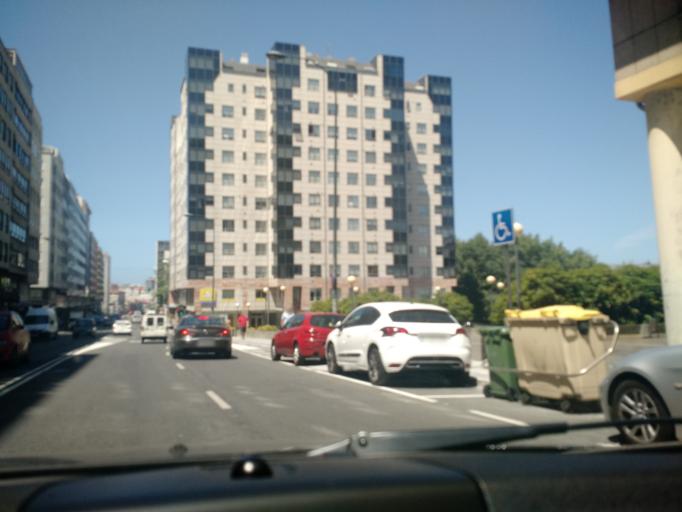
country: ES
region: Galicia
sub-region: Provincia da Coruna
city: A Coruna
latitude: 43.3631
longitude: -8.4170
